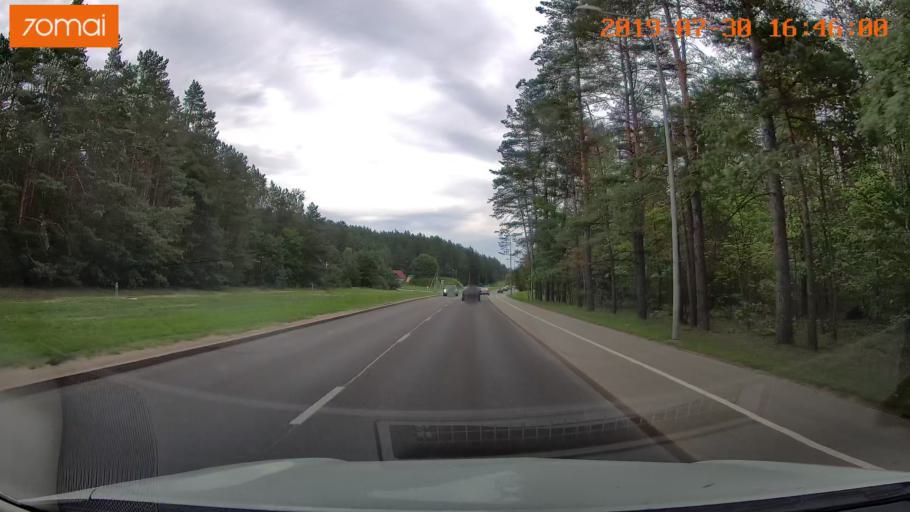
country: LT
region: Vilnius County
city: Rasos
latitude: 54.7300
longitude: 25.3542
